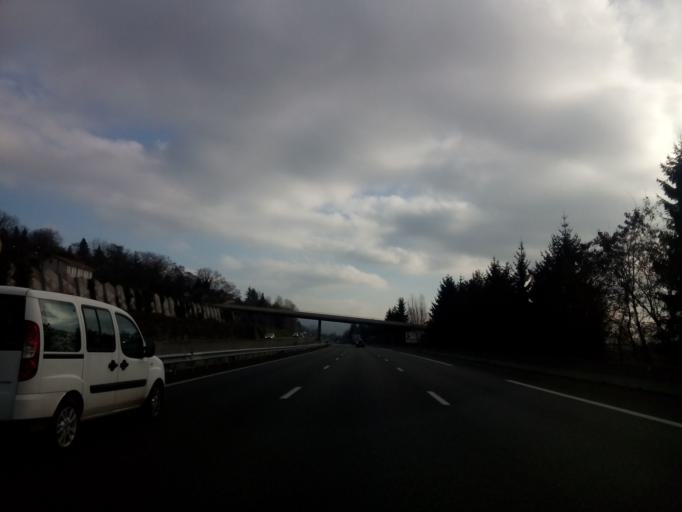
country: FR
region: Rhone-Alpes
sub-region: Departement de l'Isere
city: Bourgoin-Jallieu
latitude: 45.5959
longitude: 5.2816
